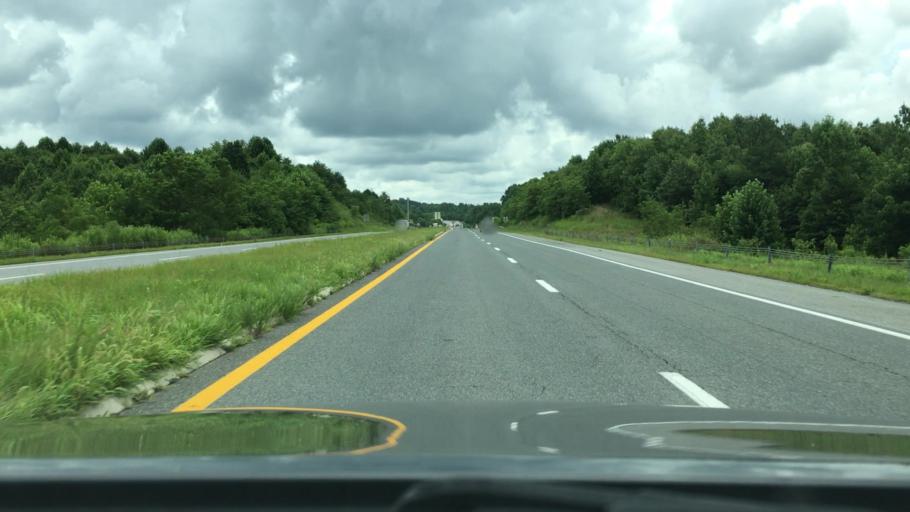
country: US
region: Virginia
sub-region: Amherst County
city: Madison Heights
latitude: 37.4111
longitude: -79.0923
